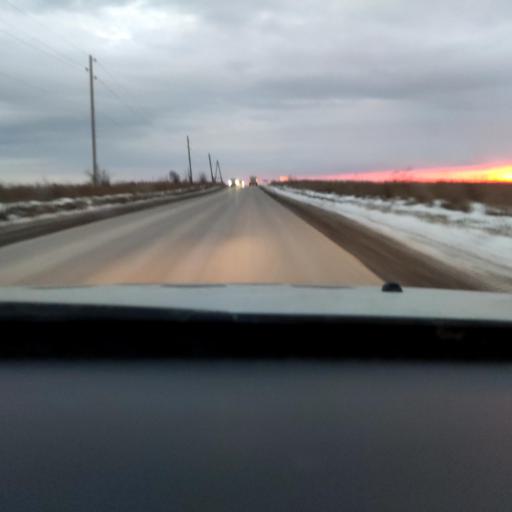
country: RU
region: Perm
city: Gamovo
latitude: 57.8852
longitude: 56.1047
